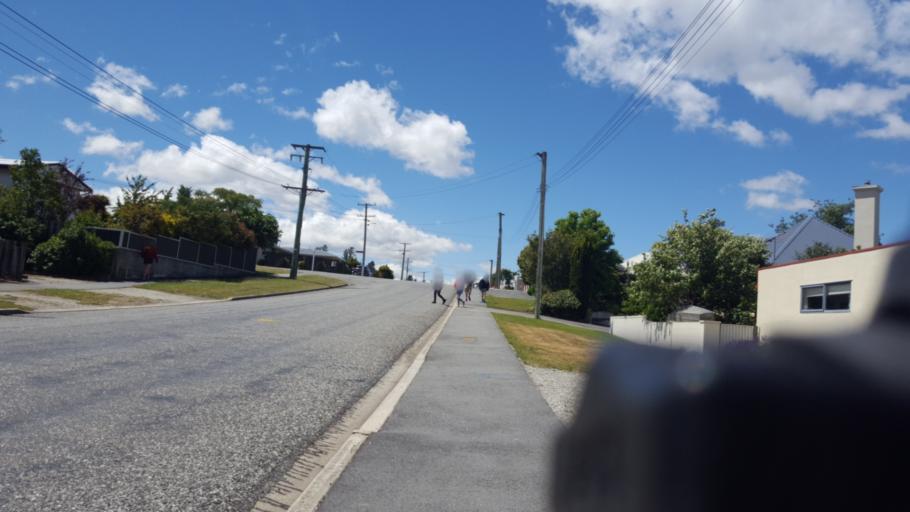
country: NZ
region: Otago
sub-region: Queenstown-Lakes District
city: Wanaka
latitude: -45.2488
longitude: 169.3939
